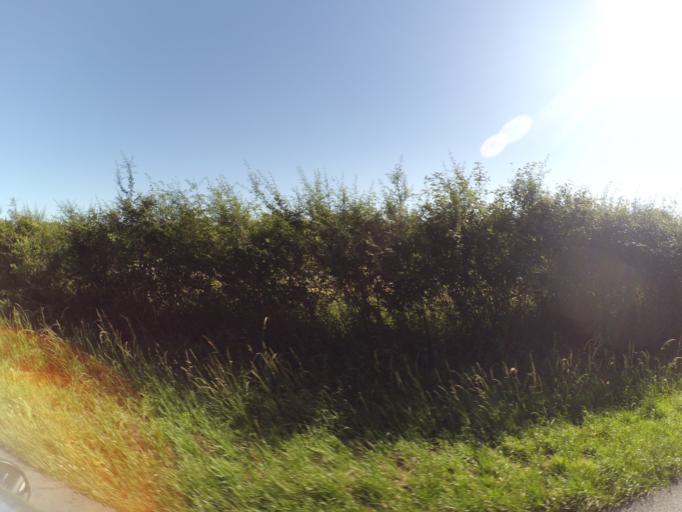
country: FR
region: Pays de la Loire
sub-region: Departement de la Vendee
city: Beaurepaire
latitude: 46.8958
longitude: -1.0609
